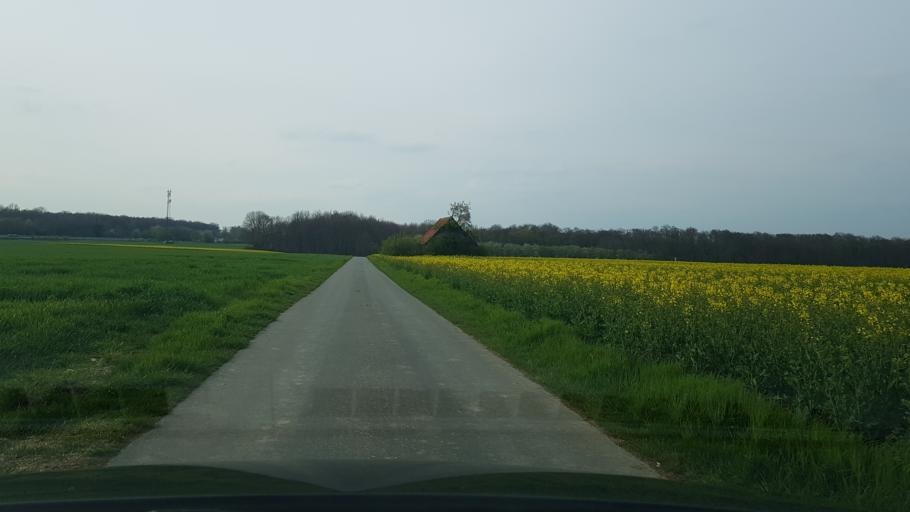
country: DE
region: North Rhine-Westphalia
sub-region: Regierungsbezirk Detmold
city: Paderborn
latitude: 51.6242
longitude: 8.7312
